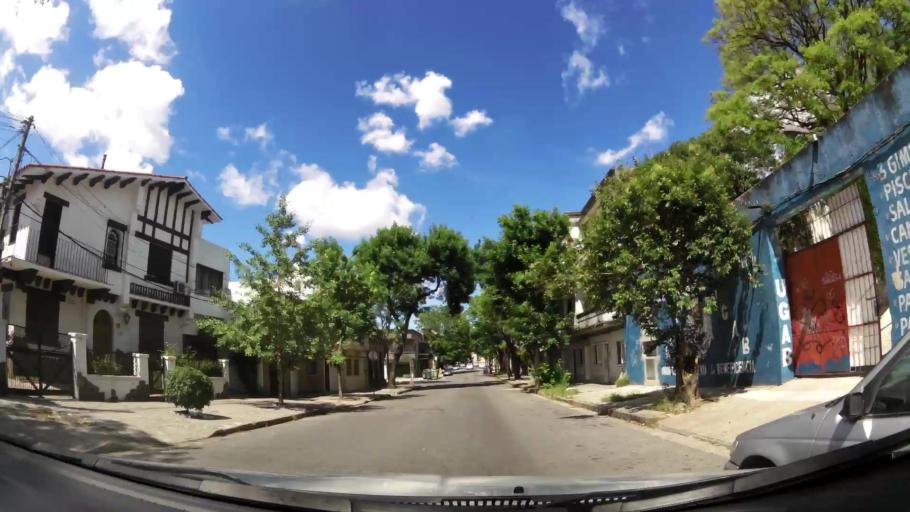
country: UY
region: Montevideo
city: Montevideo
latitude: -34.8784
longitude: -56.1948
